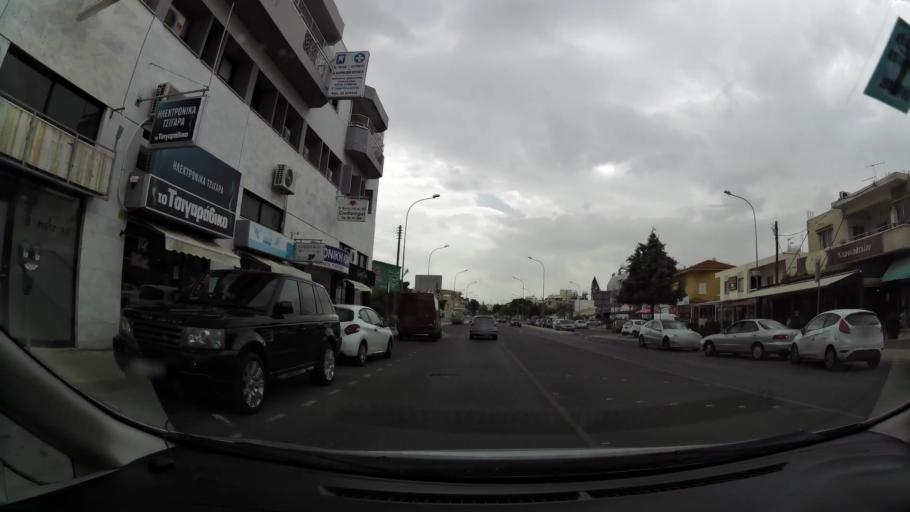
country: CY
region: Lefkosia
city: Geri
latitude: 35.1034
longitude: 33.3795
